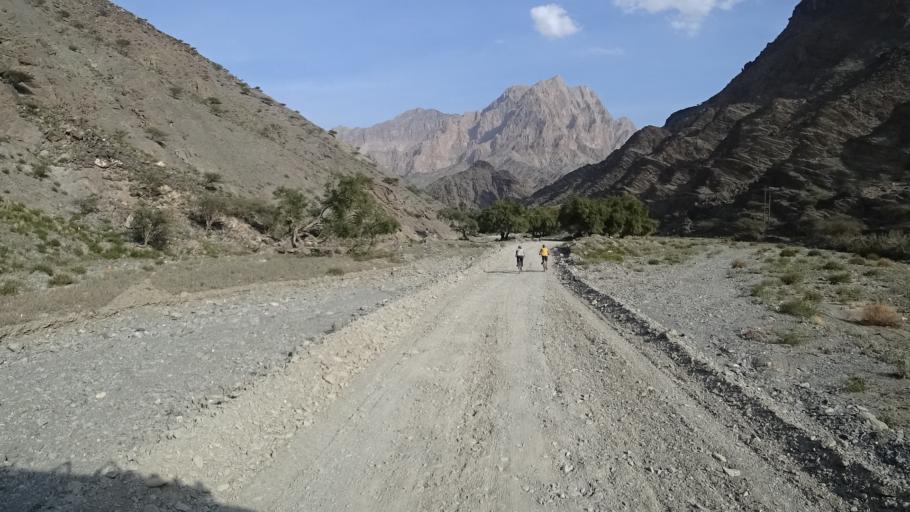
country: OM
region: Al Batinah
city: Bayt al `Awabi
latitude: 23.2569
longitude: 57.4188
